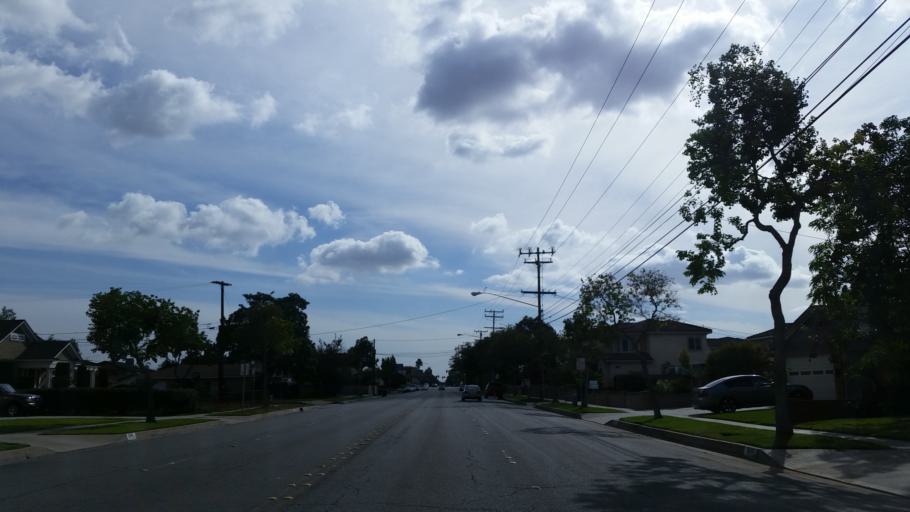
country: US
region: California
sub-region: Los Angeles County
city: Bellflower
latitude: 33.8932
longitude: -118.1341
